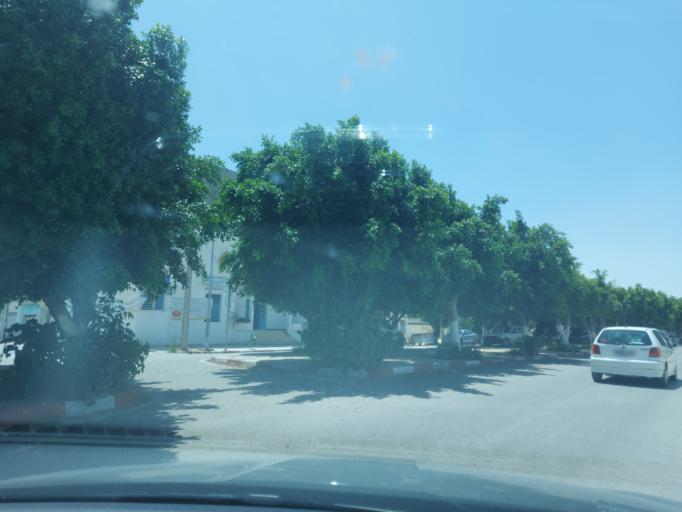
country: TN
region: Silyanah
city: Siliana
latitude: 36.0847
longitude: 9.3741
